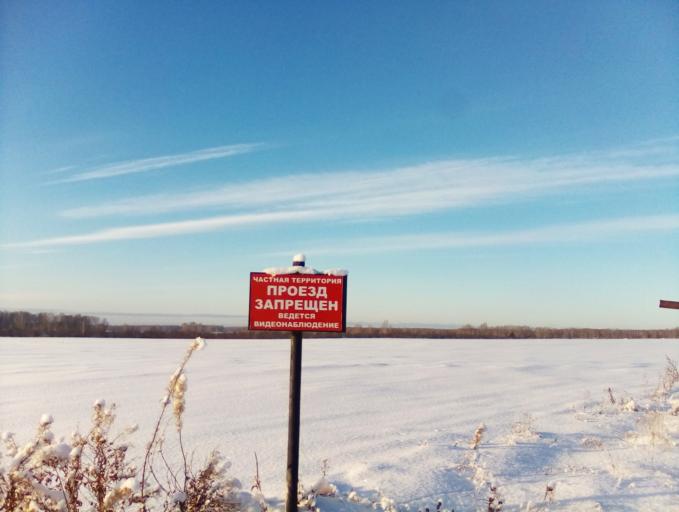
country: RU
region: Chelyabinsk
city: Poletayevo
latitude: 54.9811
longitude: 60.9479
